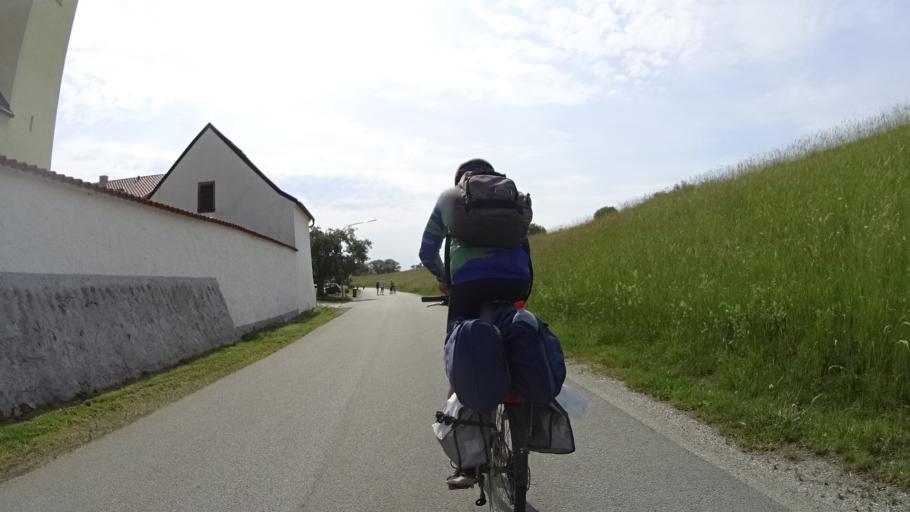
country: DE
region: Bavaria
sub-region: Lower Bavaria
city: Mariaposching
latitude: 48.8266
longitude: 12.8040
